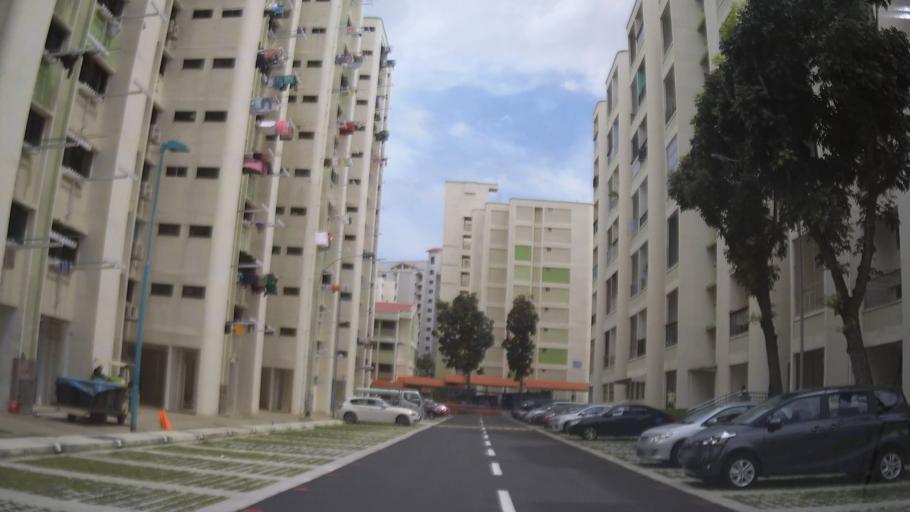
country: SG
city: Singapore
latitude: 1.3510
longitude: 103.8860
